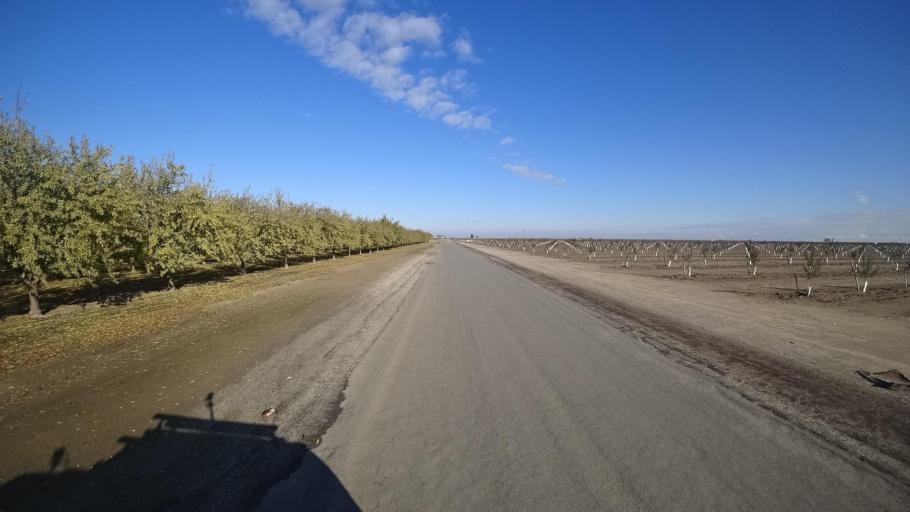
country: US
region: California
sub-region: Kern County
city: McFarland
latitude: 35.7087
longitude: -119.2941
